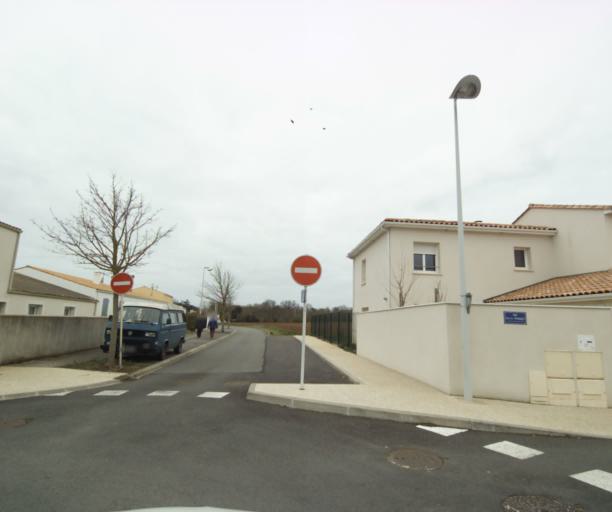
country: FR
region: Poitou-Charentes
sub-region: Departement de la Charente-Maritime
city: Lagord
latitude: 46.1896
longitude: -1.1598
